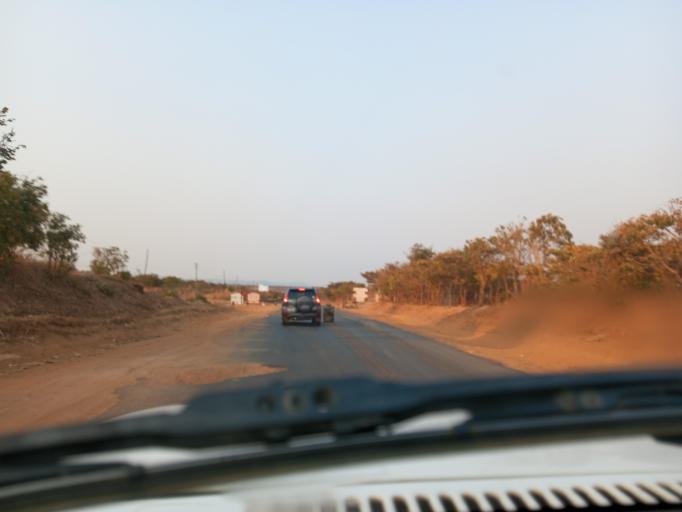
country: ZM
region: Northern
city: Mpika
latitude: -11.8930
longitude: 31.4179
